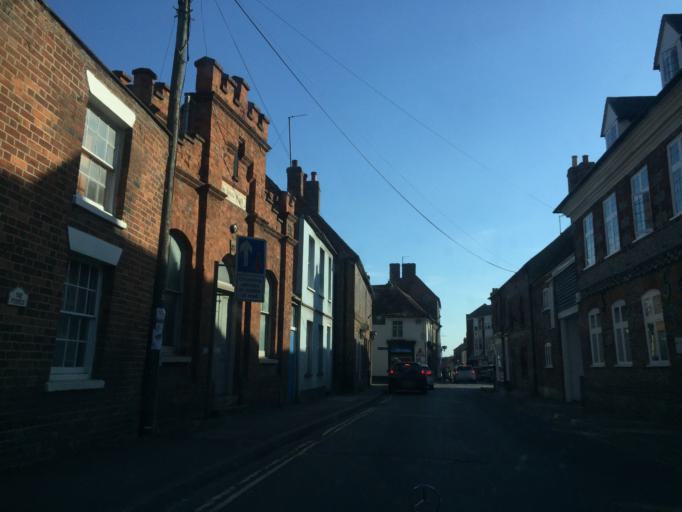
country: GB
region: England
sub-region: Oxfordshire
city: Watlington
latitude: 51.6453
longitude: -1.0037
